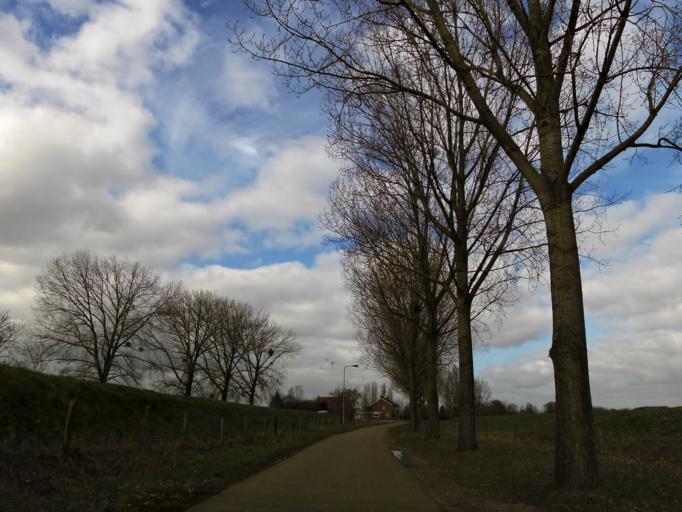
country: NL
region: Limburg
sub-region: Gemeente Sittard-Geleen
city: Born
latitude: 51.0641
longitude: 5.8035
